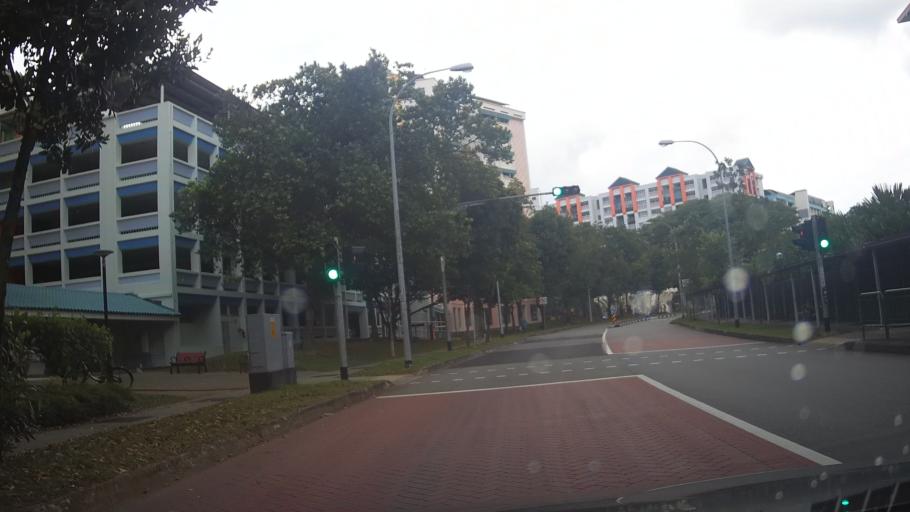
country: MY
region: Johor
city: Johor Bahru
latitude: 1.4420
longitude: 103.7892
